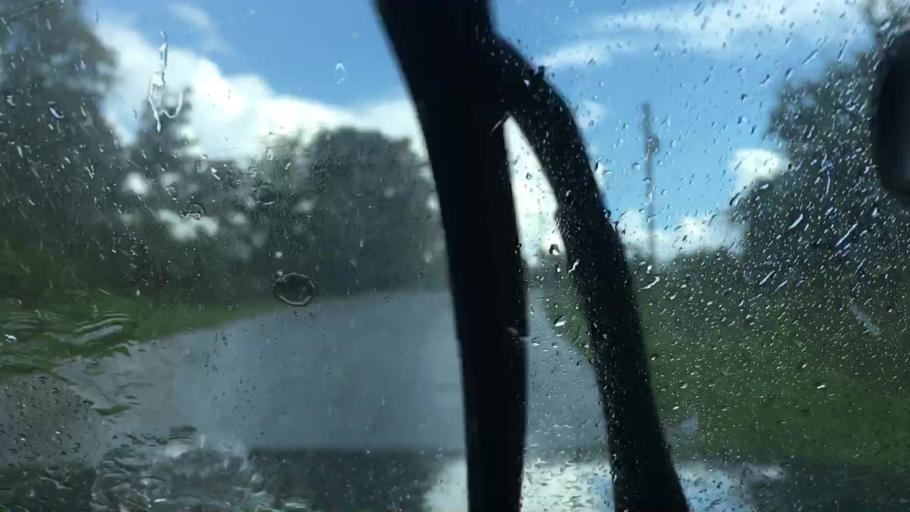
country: US
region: Georgia
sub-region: Bibb County
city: West Point
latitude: 32.8178
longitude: -83.7950
